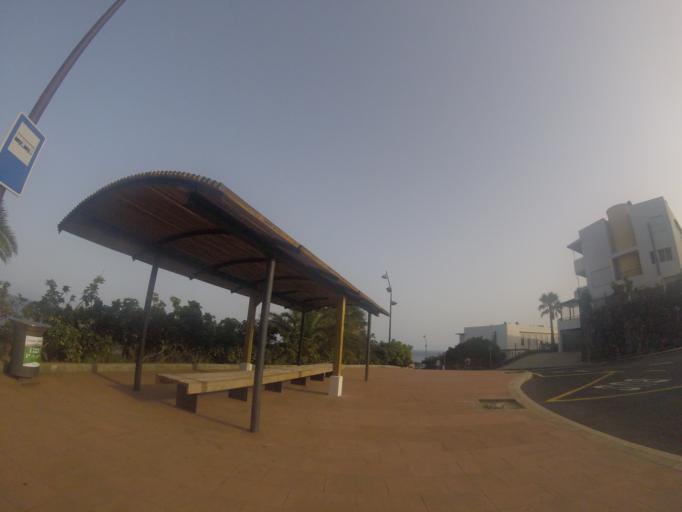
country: ES
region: Canary Islands
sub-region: Provincia de Santa Cruz de Tenerife
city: Candelaria
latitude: 28.4023
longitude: -16.3194
